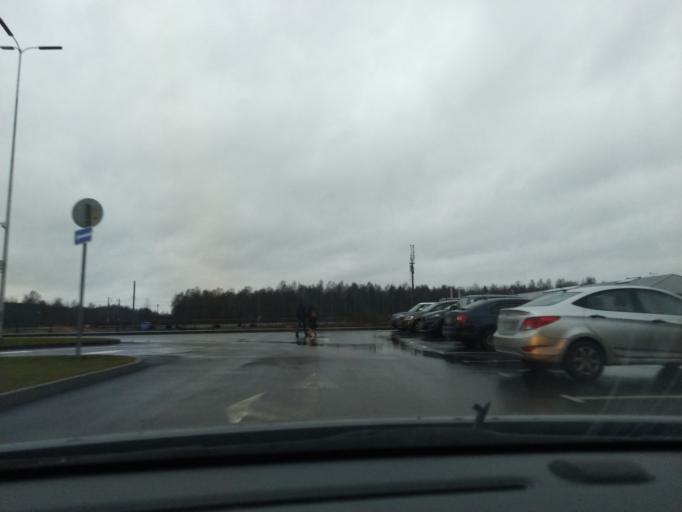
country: RU
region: St.-Petersburg
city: Gorelovo
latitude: 59.7939
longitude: 30.1468
